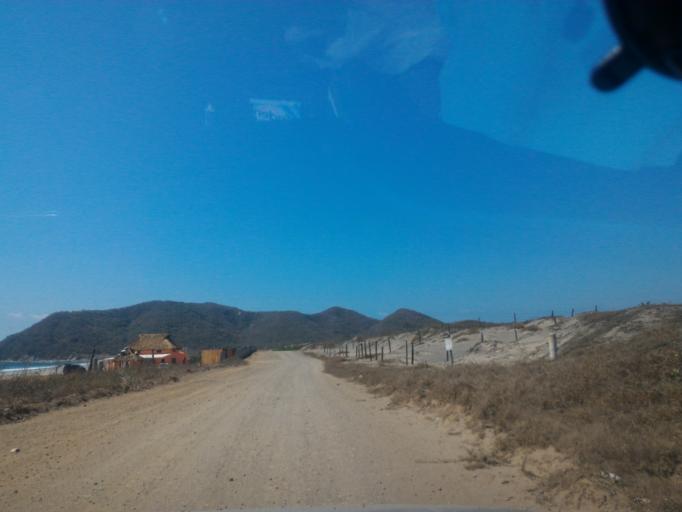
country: MX
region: Michoacan
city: Coahuayana Viejo
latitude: 18.5916
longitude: -103.6892
